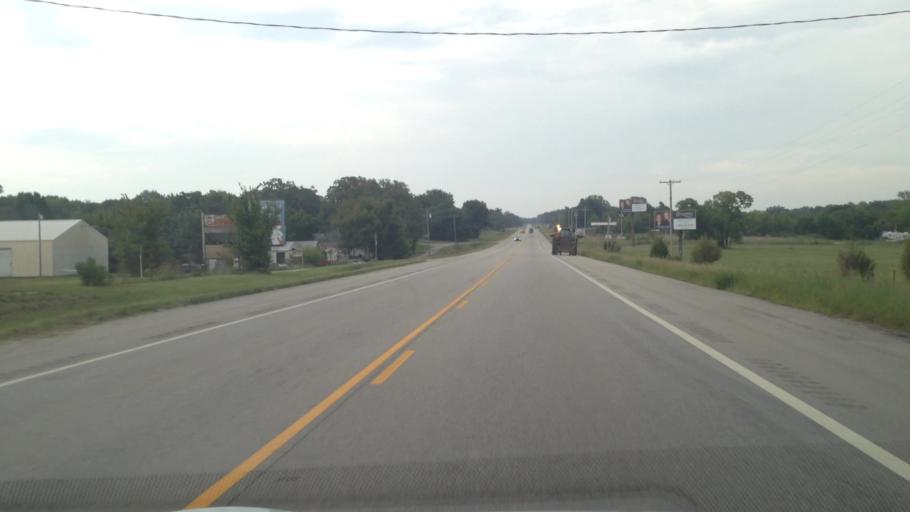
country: US
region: Kansas
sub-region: Cherokee County
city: Galena
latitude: 37.0236
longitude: -94.6524
